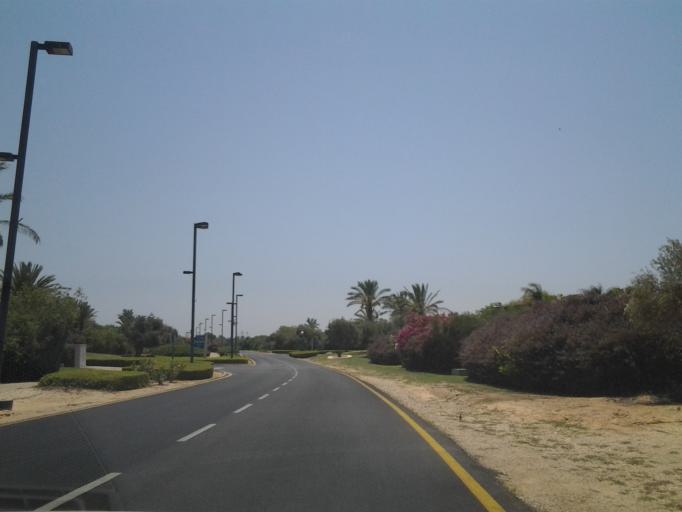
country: IL
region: Haifa
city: Qesarya
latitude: 32.5291
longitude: 34.9072
